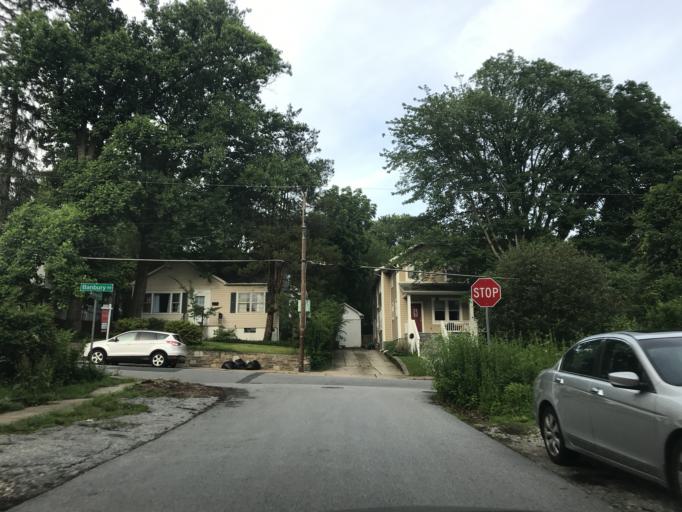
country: US
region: Maryland
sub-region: Baltimore County
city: Towson
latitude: 39.3745
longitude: -76.5974
